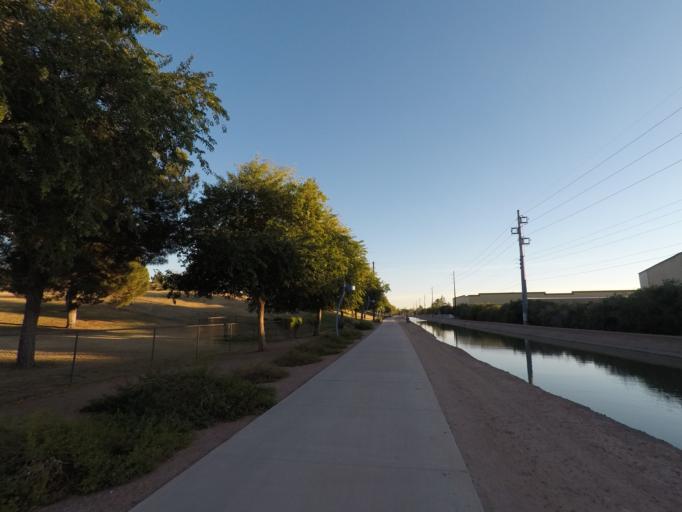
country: US
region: Arizona
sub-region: Maricopa County
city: Guadalupe
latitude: 33.3711
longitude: -111.9400
